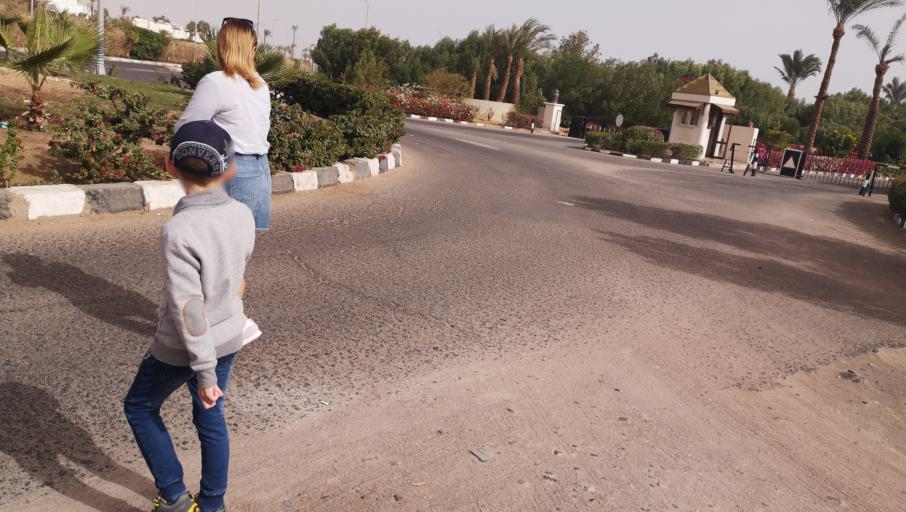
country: EG
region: South Sinai
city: Sharm el-Sheikh
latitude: 27.8652
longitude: 34.3161
